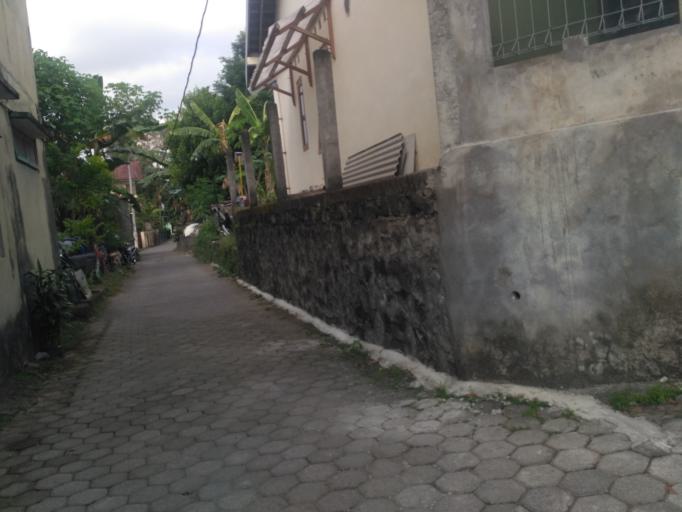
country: ID
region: Daerah Istimewa Yogyakarta
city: Melati
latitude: -7.7527
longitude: 110.3662
